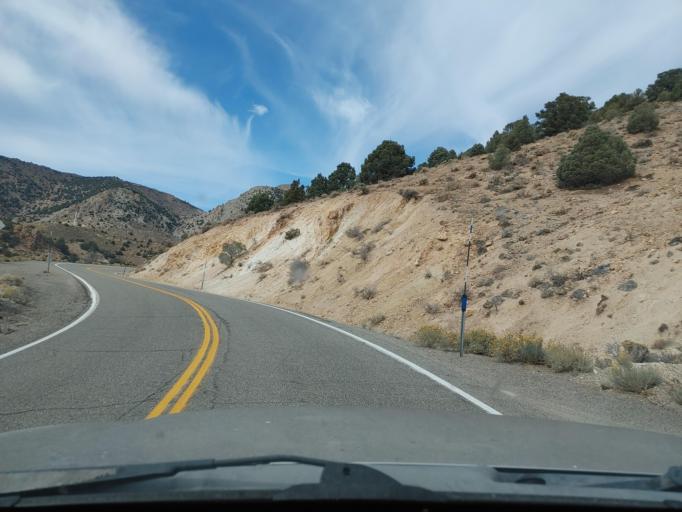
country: US
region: Nevada
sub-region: Storey County
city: Virginia City
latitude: 39.2924
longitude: -119.6422
